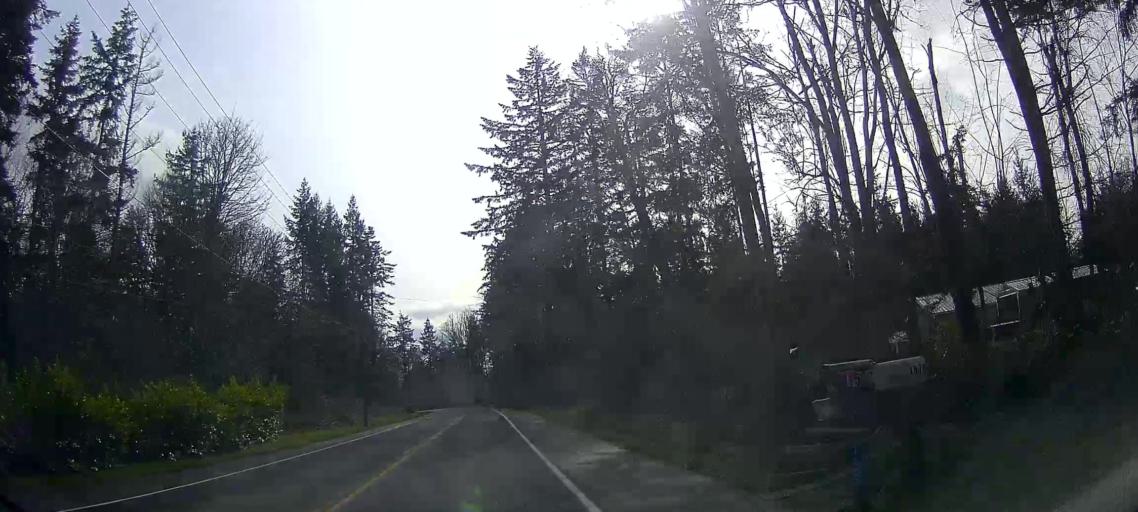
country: US
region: Washington
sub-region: Island County
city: Camano
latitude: 48.1535
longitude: -122.4748
